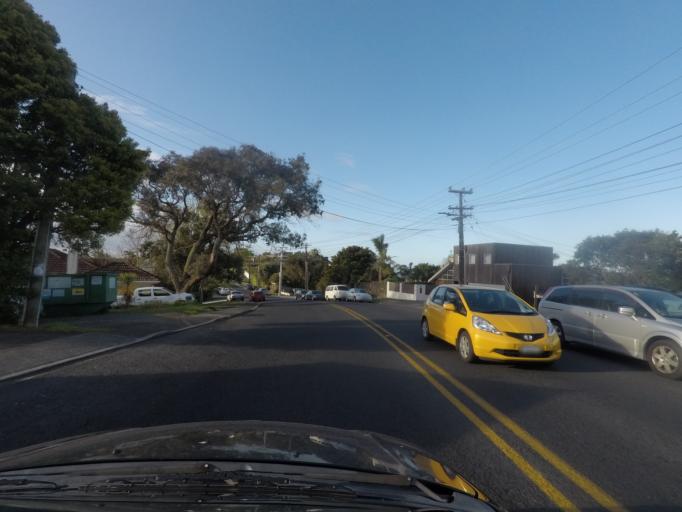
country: NZ
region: Auckland
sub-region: Auckland
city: Waitakere
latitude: -36.9192
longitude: 174.6579
